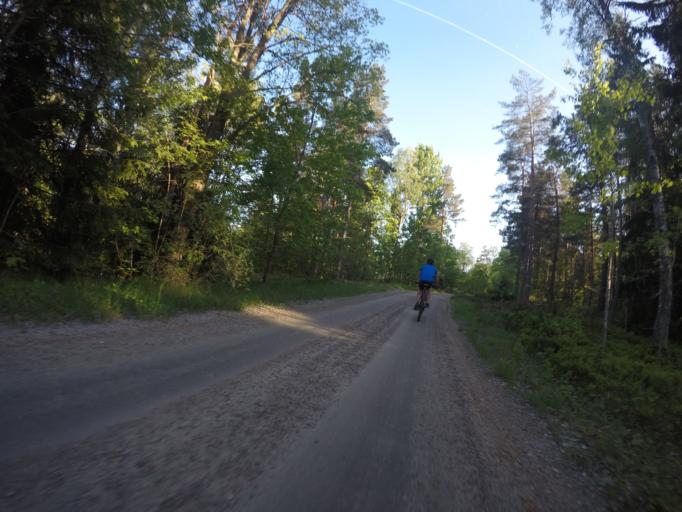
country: SE
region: Soedermanland
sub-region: Eskilstuna Kommun
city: Eskilstuna
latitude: 59.3487
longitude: 16.5340
